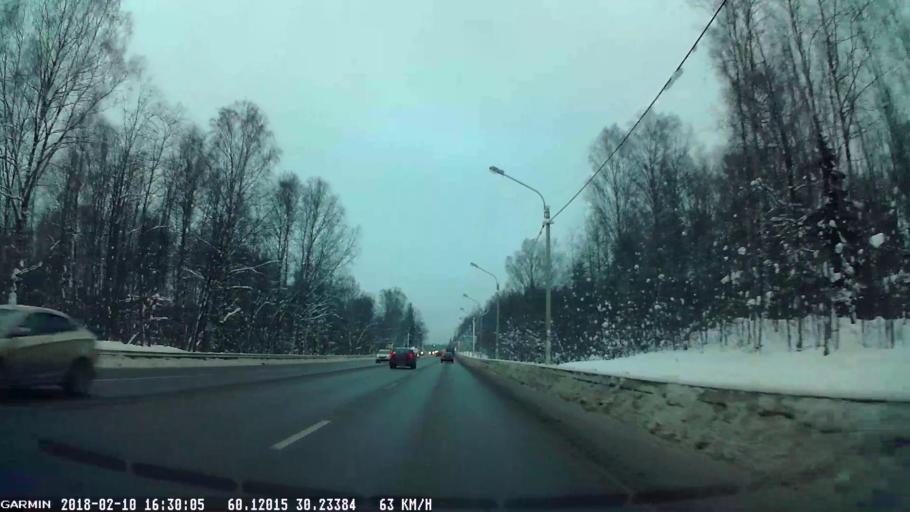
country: RU
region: St.-Petersburg
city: Levashovo
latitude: 60.1207
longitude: 30.2333
